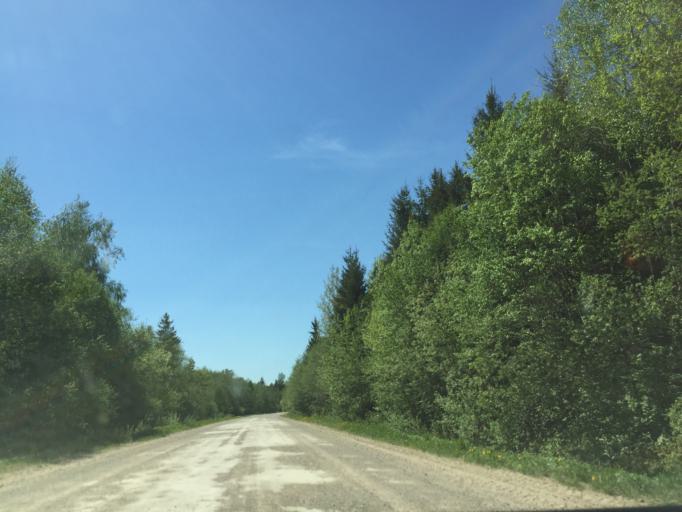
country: LV
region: Kegums
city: Kegums
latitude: 56.8712
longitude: 24.7757
